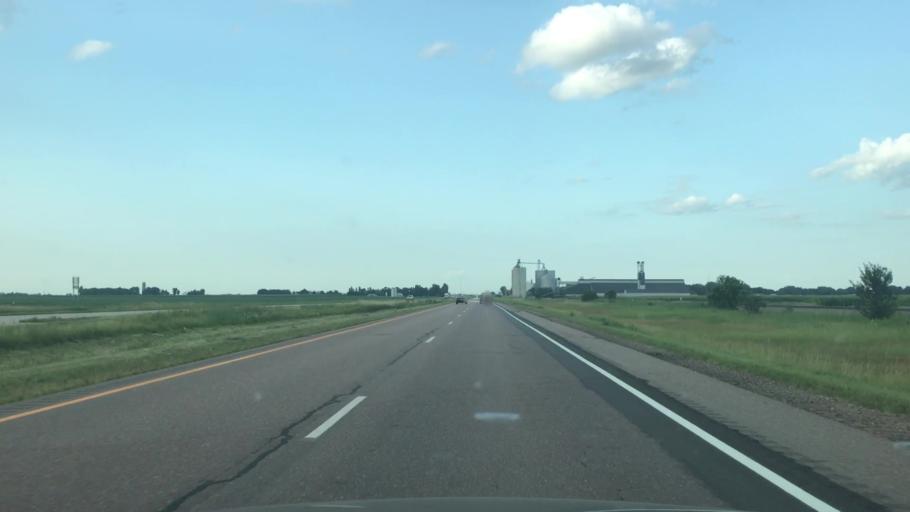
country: US
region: Minnesota
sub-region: Nobles County
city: Worthington
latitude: 43.6891
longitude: -95.4861
